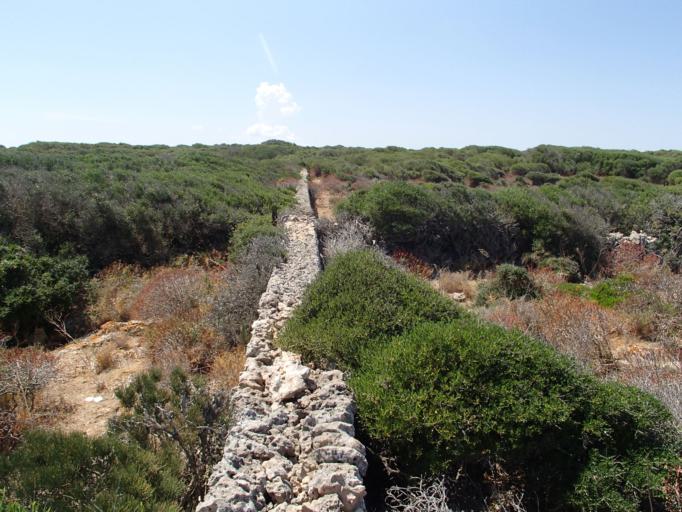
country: ES
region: Balearic Islands
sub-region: Illes Balears
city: Es Castell
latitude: 39.8479
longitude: 4.3043
